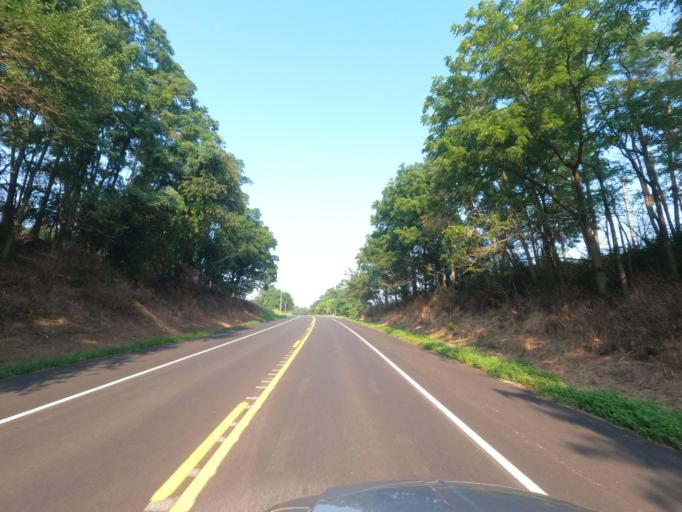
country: US
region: Pennsylvania
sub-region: Franklin County
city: Wayne Heights
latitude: 39.7078
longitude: -77.5847
